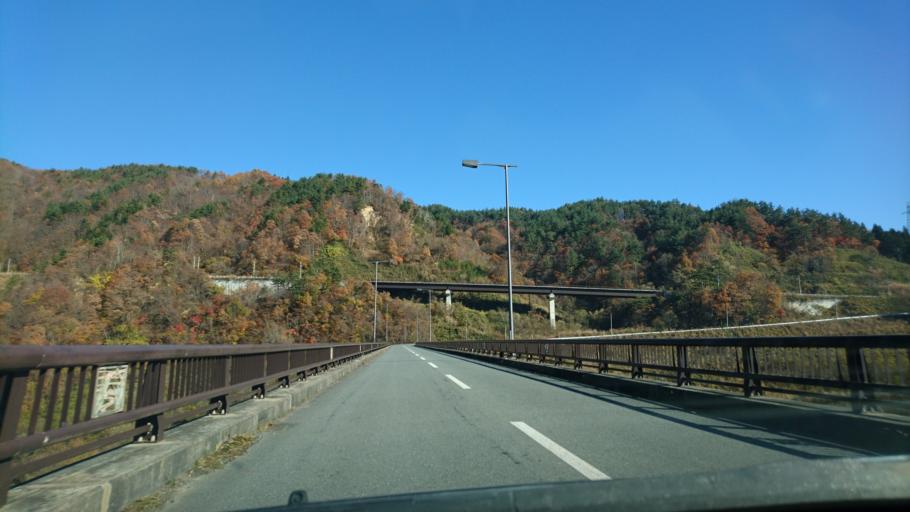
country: JP
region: Iwate
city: Mizusawa
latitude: 39.1219
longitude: 140.9338
